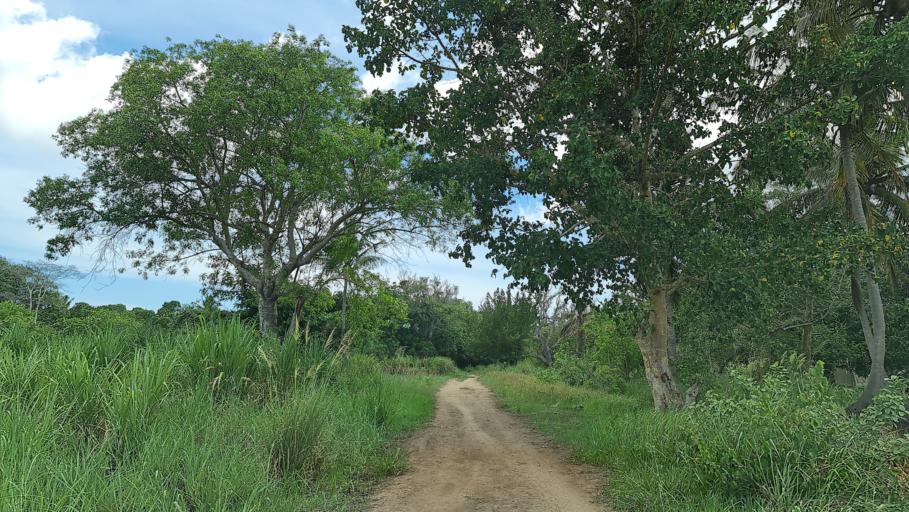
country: MZ
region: Zambezia
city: Quelimane
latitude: -17.5864
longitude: 37.3950
